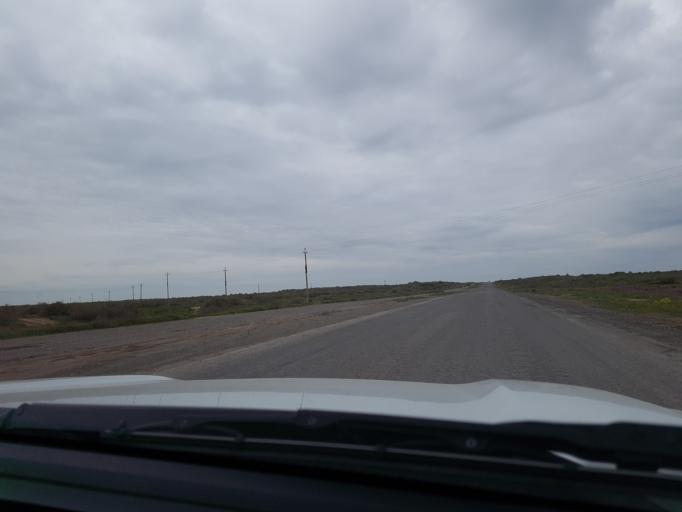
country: TM
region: Mary
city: Bayramaly
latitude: 37.9185
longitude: 62.6230
